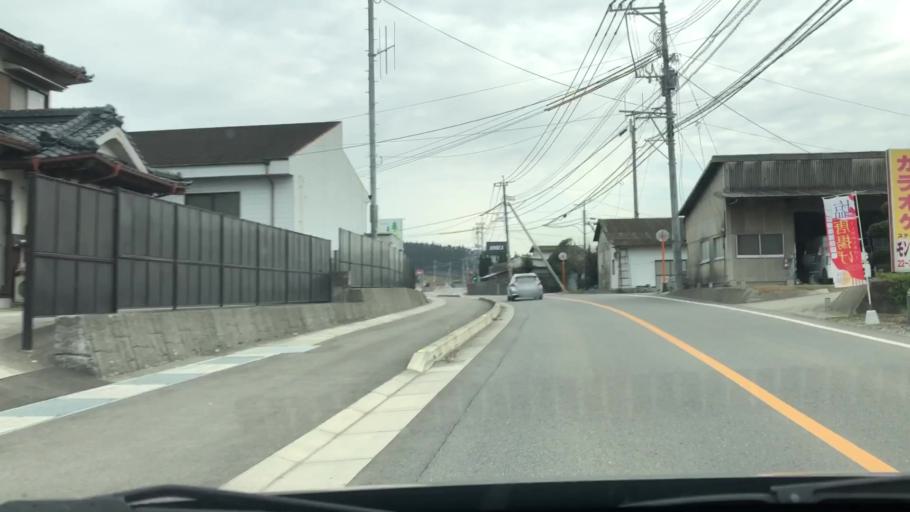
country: JP
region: Oita
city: Takedamachi
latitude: 32.9978
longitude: 131.6173
